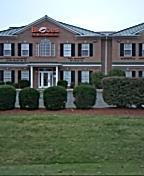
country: US
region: Kentucky
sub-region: Jefferson County
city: Middletown
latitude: 38.2474
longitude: -85.5310
